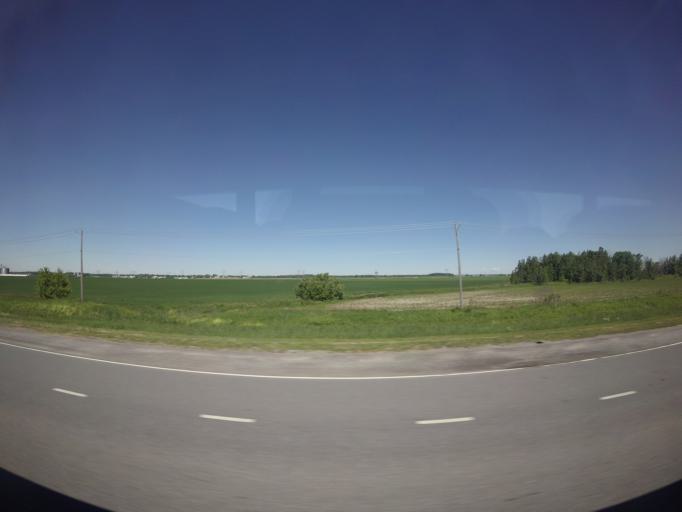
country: CA
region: Quebec
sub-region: Mauricie
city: Saint-Germain-de-Grantham
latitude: 45.7564
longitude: -72.7064
